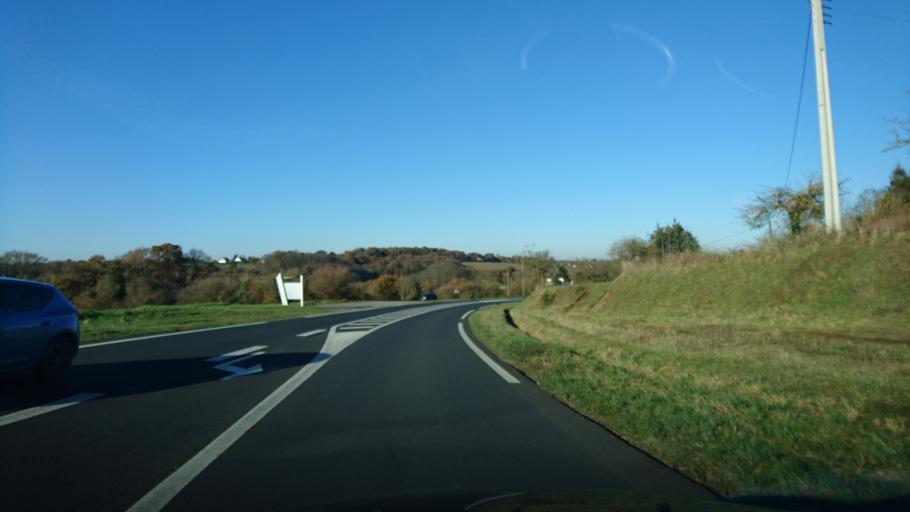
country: FR
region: Brittany
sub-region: Departement des Cotes-d'Armor
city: Pledran
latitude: 48.4588
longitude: -2.7558
